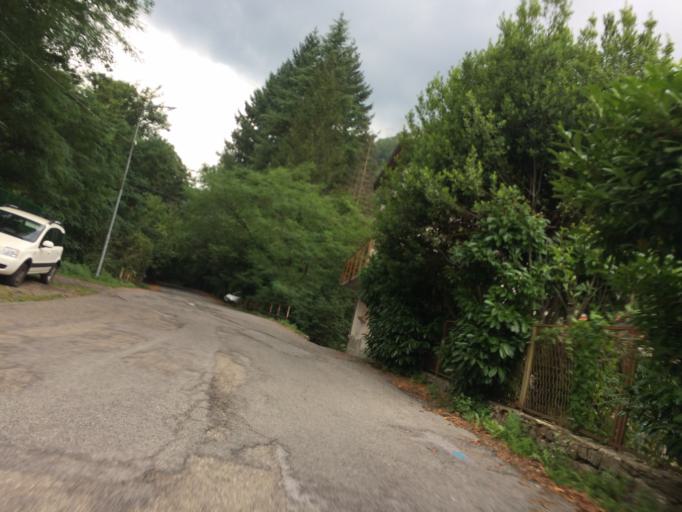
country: IT
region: Liguria
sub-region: Provincia di Imperia
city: Molini di Triora
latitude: 43.9868
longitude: 7.7743
